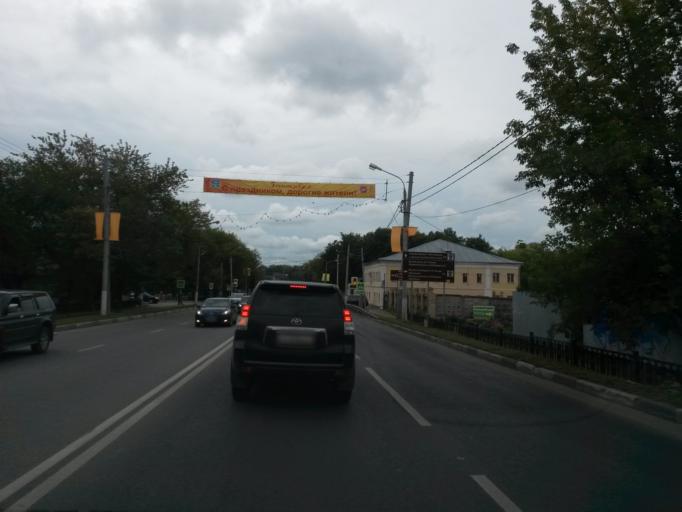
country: RU
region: Moskovskaya
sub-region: Chekhovskiy Rayon
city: Chekhov
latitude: 55.1432
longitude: 37.4526
